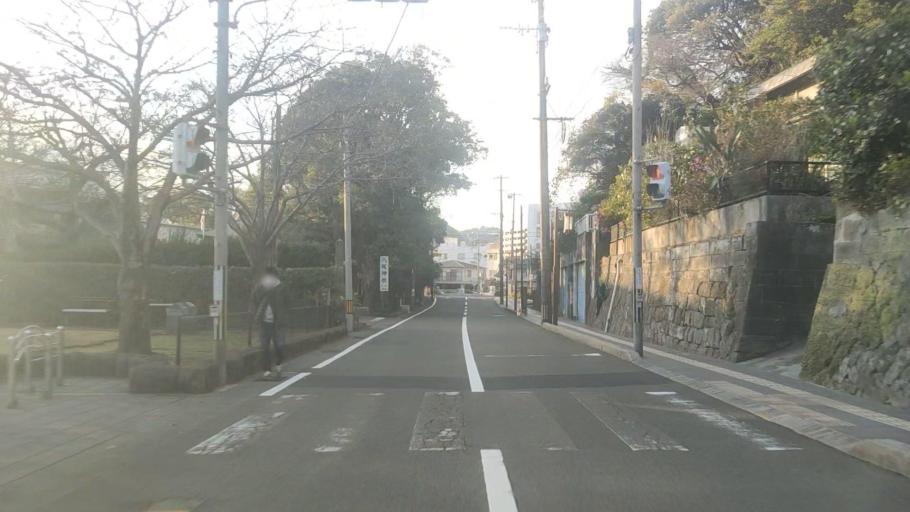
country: JP
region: Kagoshima
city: Kagoshima-shi
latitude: 31.6054
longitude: 130.5690
